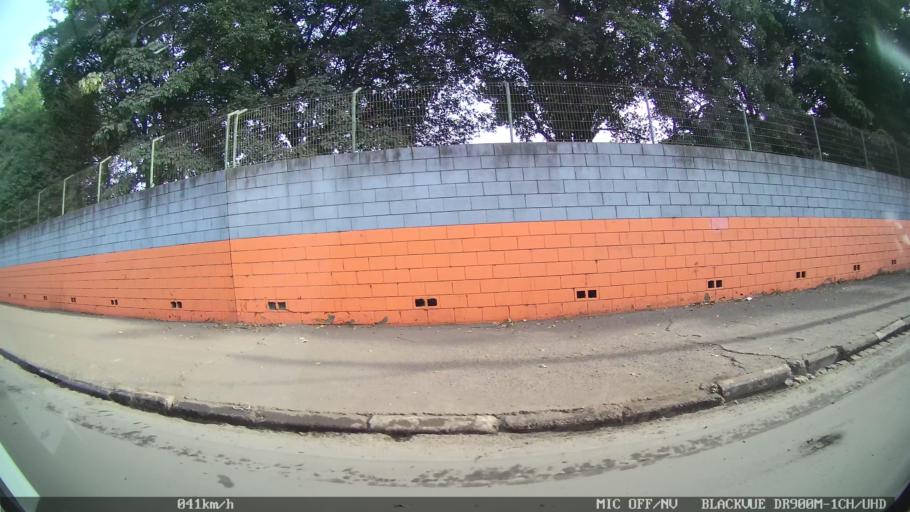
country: BR
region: Sao Paulo
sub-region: Piracicaba
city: Piracicaba
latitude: -22.6995
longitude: -47.6550
